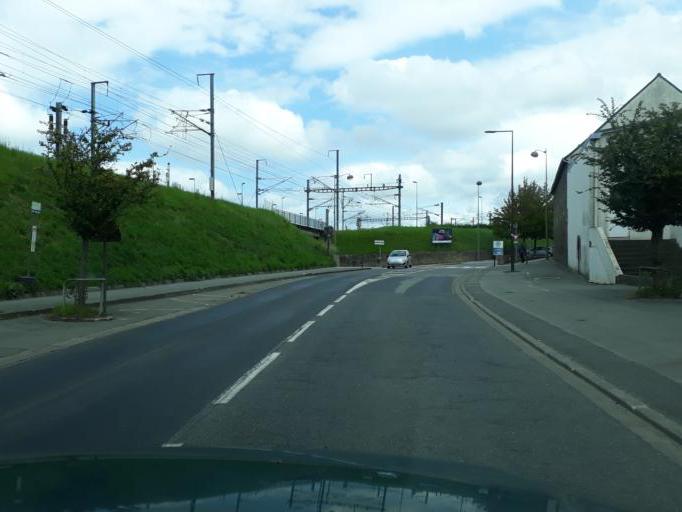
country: FR
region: Brittany
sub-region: Departement des Cotes-d'Armor
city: Lamballe
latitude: 48.4656
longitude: -2.5148
